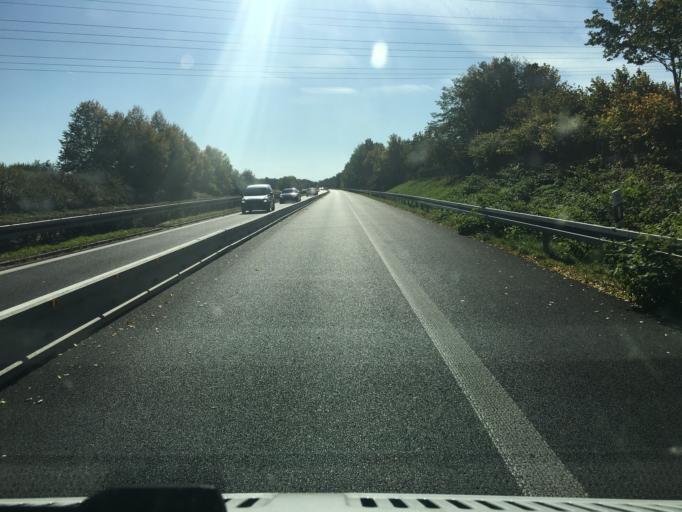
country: DE
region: Saxony
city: Zwickau
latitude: 50.7545
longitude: 12.5020
